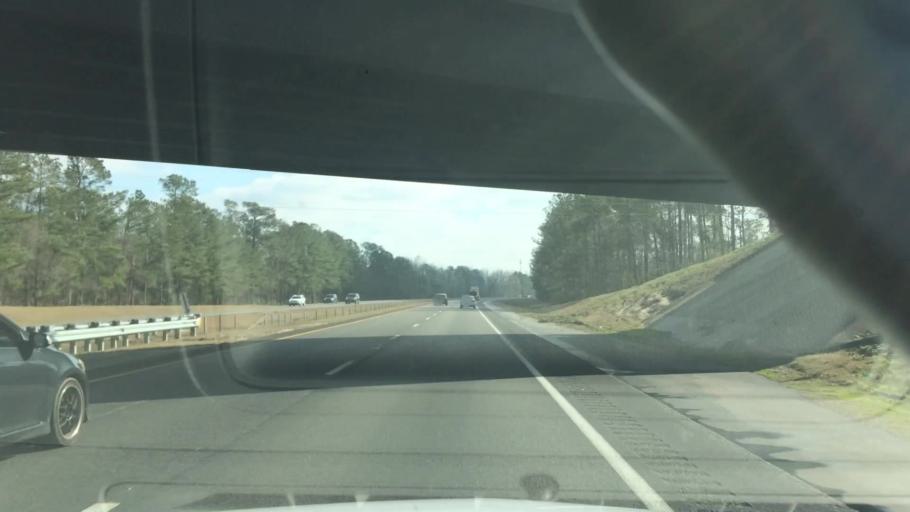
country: US
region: North Carolina
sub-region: Pender County
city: Burgaw
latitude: 34.6119
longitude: -77.9206
